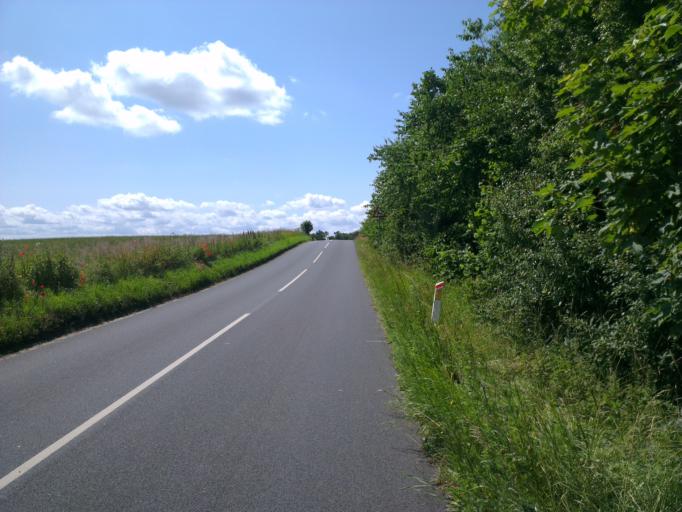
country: DK
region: Capital Region
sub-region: Frederikssund Kommune
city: Skibby
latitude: 55.7679
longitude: 11.9052
